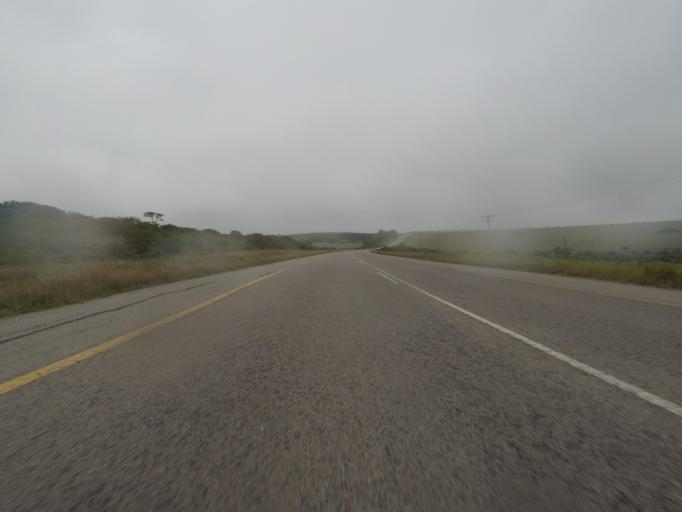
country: ZA
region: Eastern Cape
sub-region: Cacadu District Municipality
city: Grahamstown
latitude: -33.6428
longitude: 26.3731
